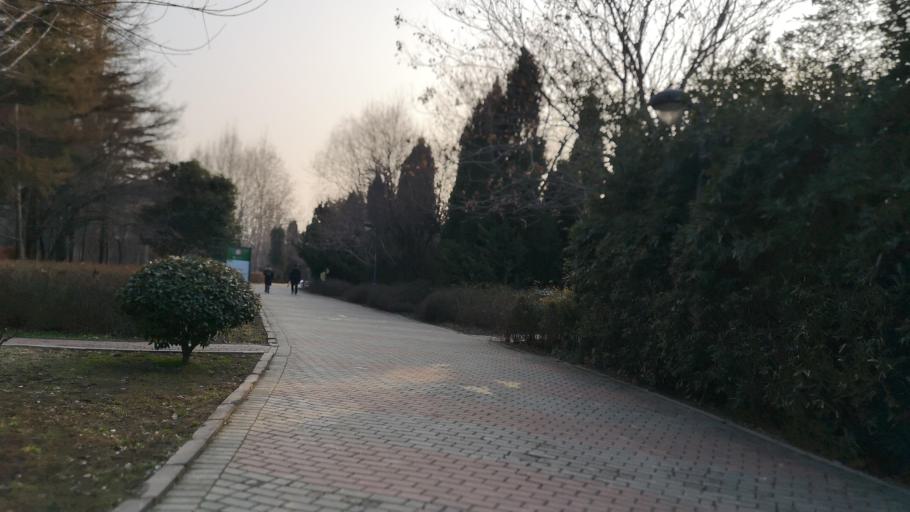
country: CN
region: Henan Sheng
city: Zhongyuanlu
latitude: 35.7441
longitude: 115.0625
